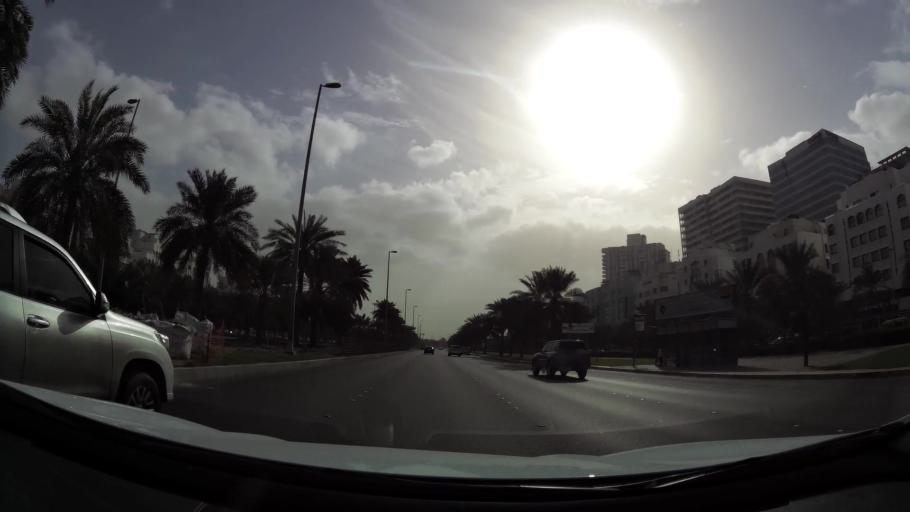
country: AE
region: Abu Dhabi
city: Abu Dhabi
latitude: 24.4333
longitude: 54.4345
